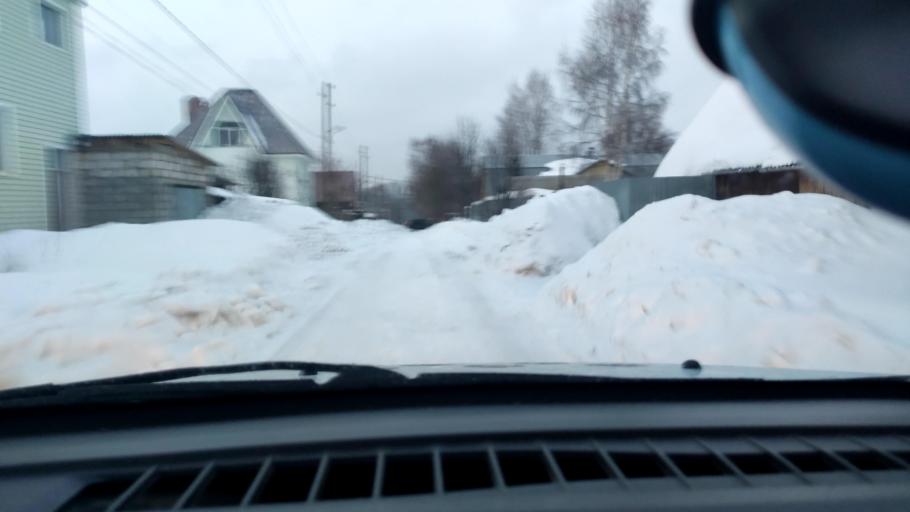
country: RU
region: Perm
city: Perm
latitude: 58.0186
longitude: 56.3174
